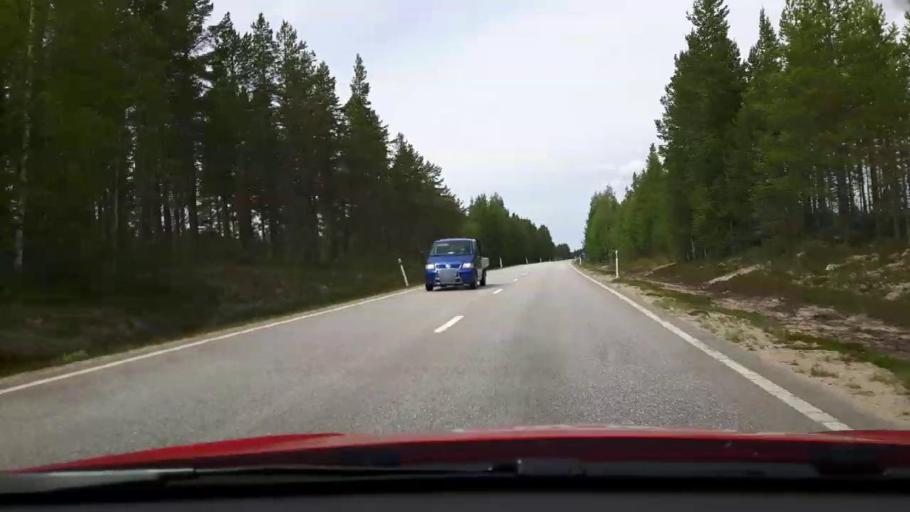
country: SE
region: Jaemtland
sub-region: Harjedalens Kommun
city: Sveg
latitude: 62.1136
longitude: 14.1805
